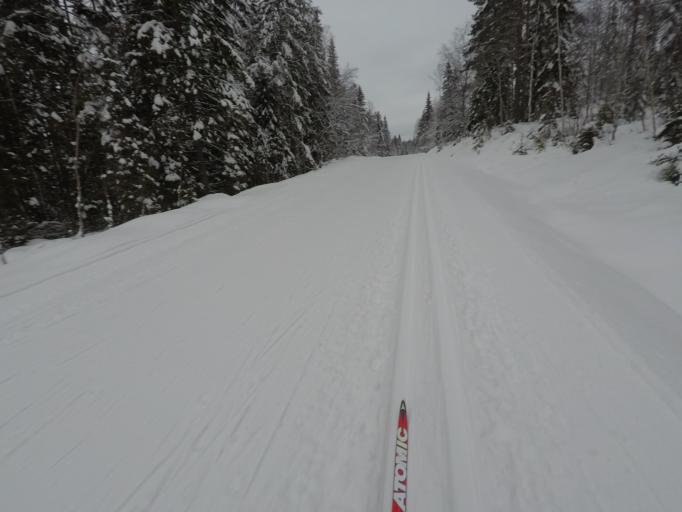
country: SE
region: Dalarna
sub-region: Ludvika Kommun
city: Abborrberget
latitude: 60.1517
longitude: 14.4896
